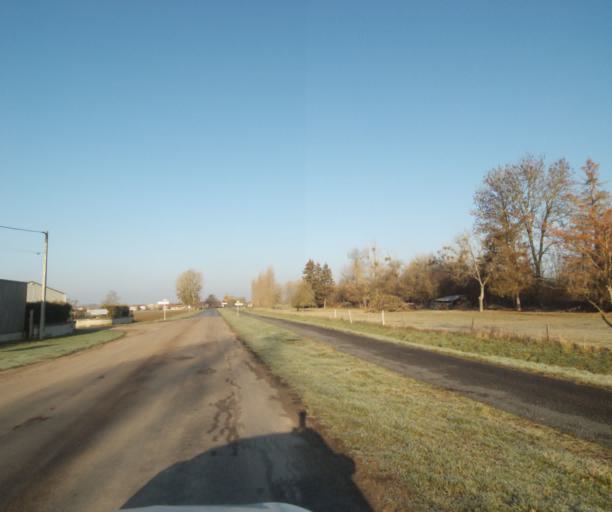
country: FR
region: Champagne-Ardenne
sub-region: Departement de la Haute-Marne
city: Montier-en-Der
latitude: 48.4757
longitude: 4.7625
